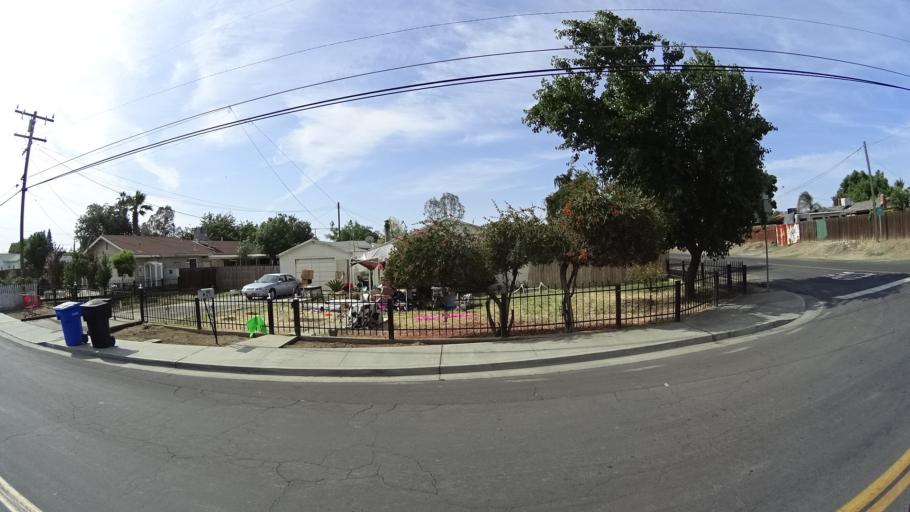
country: US
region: California
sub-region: Kings County
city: Hanford
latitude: 36.3177
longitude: -119.6639
